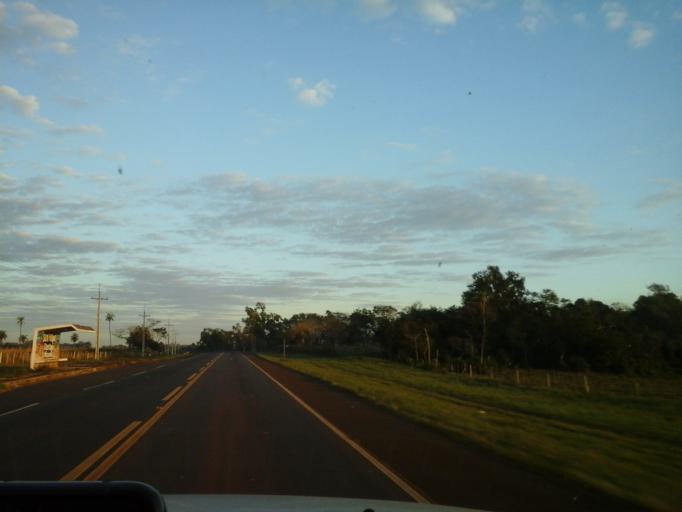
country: PY
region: Misiones
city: Santiago
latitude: -27.0375
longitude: -56.6687
